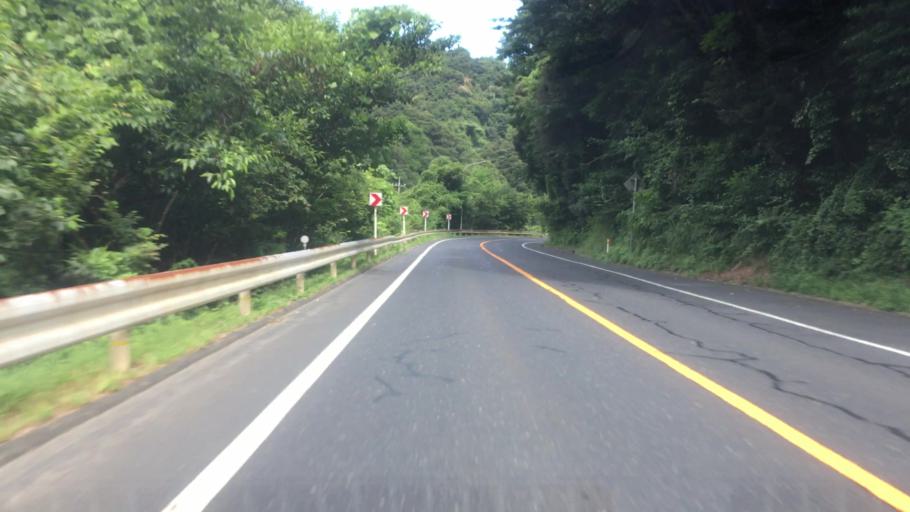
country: JP
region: Tottori
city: Tottori
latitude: 35.5953
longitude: 134.3528
